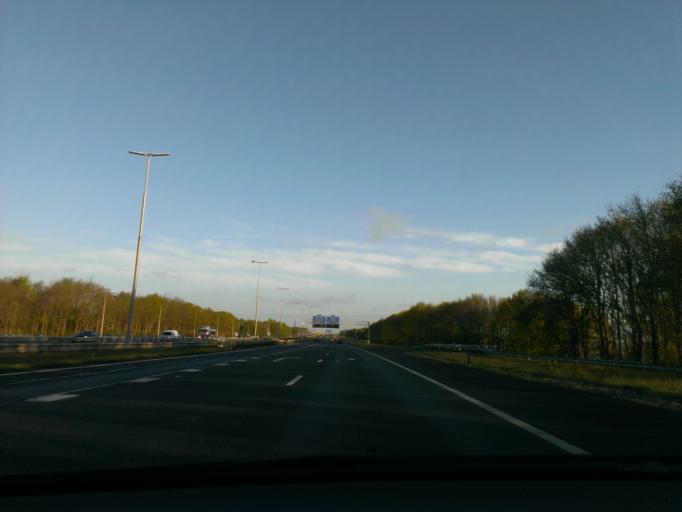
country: NL
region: Gelderland
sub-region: Gemeente Hattem
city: Hattem
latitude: 52.4808
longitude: 6.0316
